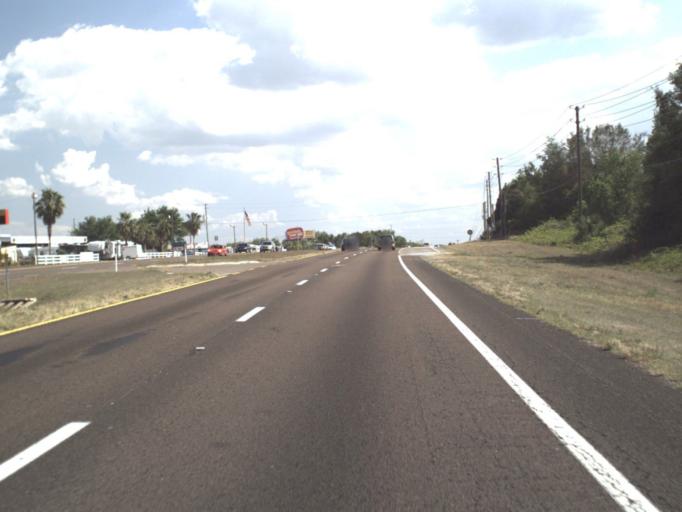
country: US
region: Florida
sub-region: Lake County
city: Minneola
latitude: 28.6065
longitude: -81.7569
